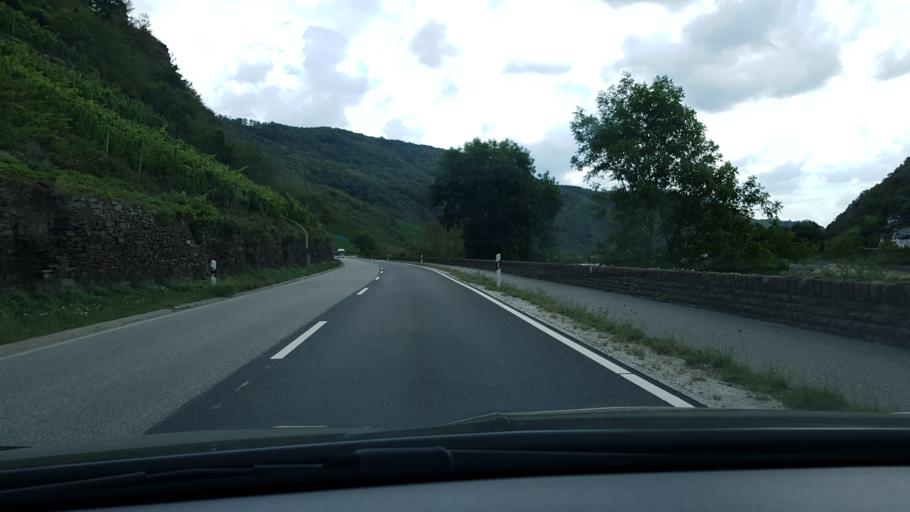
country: DE
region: Rheinland-Pfalz
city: Niederfell
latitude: 50.2823
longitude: 7.4584
